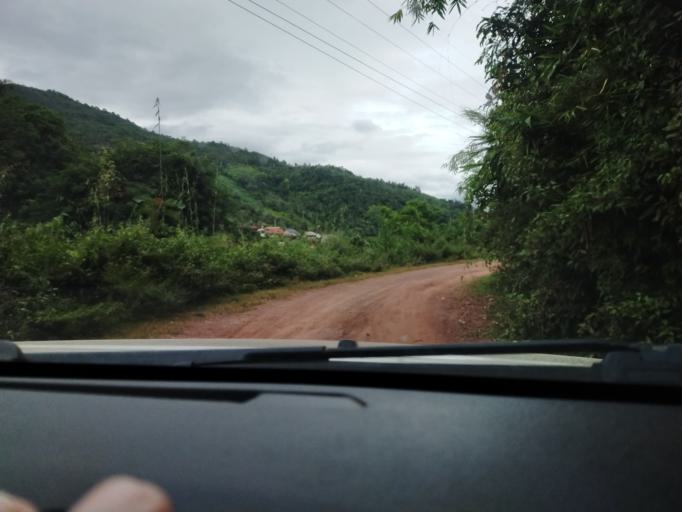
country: TH
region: Nan
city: Chaloem Phra Kiat
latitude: 19.7719
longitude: 101.3488
